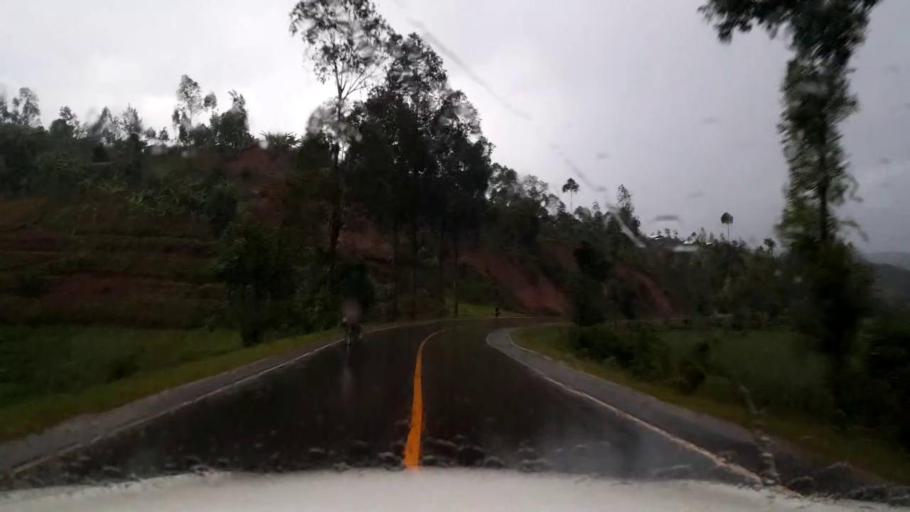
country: RW
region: Northern Province
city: Musanze
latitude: -1.5343
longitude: 29.6700
